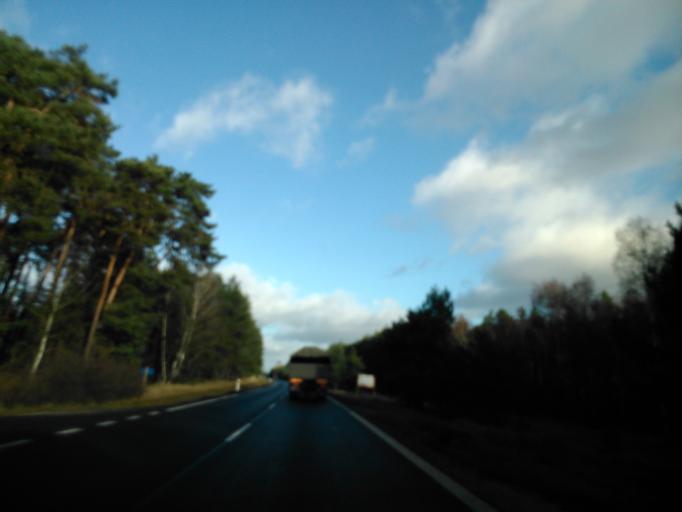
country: PL
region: Kujawsko-Pomorskie
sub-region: Powiat torunski
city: Wielka Nieszawka
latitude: 52.9600
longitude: 18.5350
